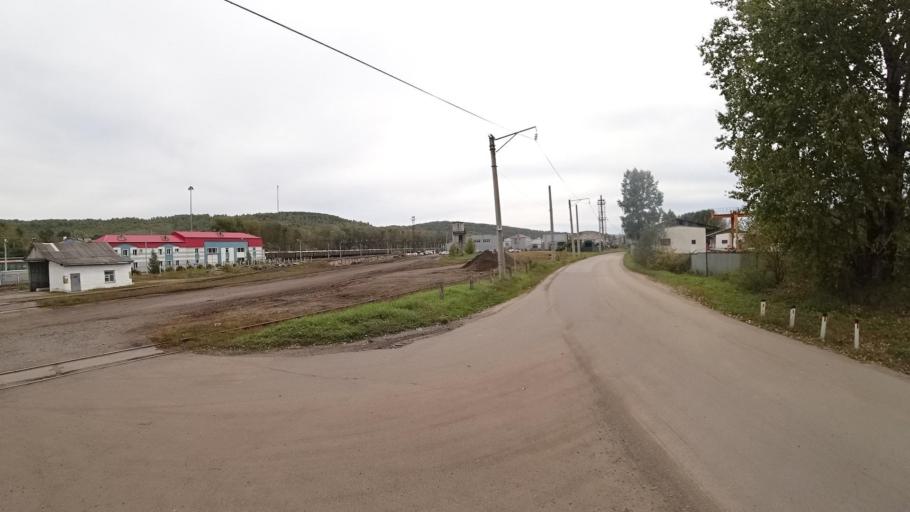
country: RU
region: Jewish Autonomous Oblast
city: Khingansk
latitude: 49.0209
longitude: 131.0547
